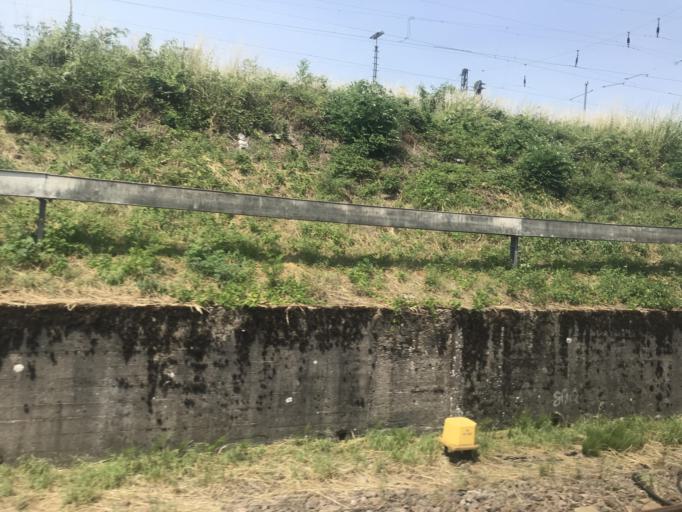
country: DE
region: Saarland
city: Saarbrucken
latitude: 49.2451
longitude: 7.0031
